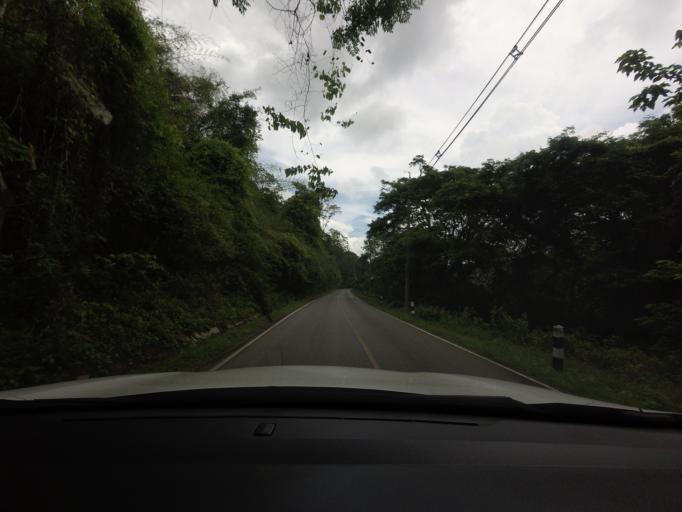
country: TH
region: Nakhon Ratchasima
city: Pak Chong
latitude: 14.5015
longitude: 101.3828
